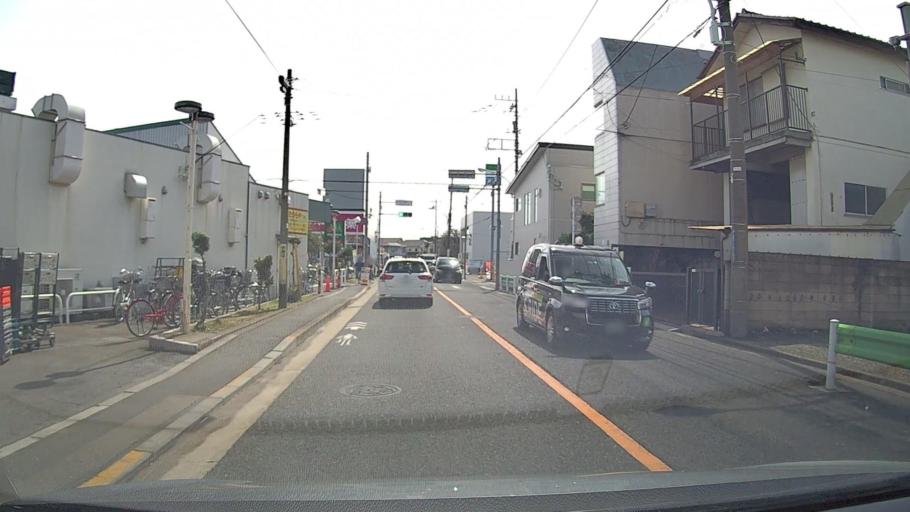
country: JP
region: Tokyo
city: Tanashicho
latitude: 35.7434
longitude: 139.5511
